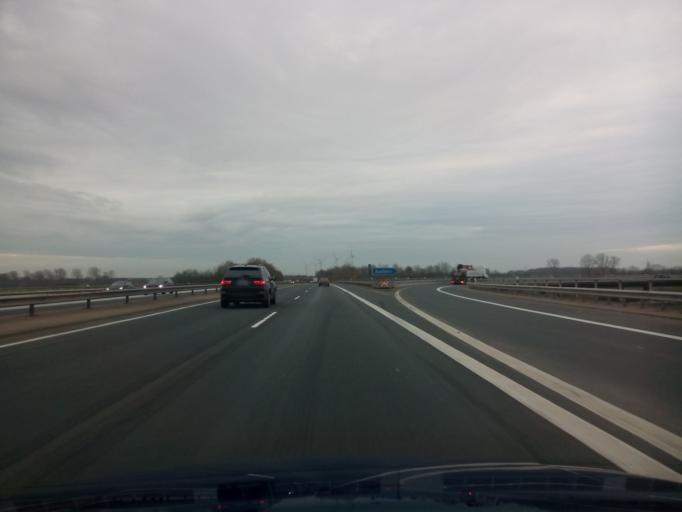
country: DE
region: Lower Saxony
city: Loxstedt
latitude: 53.4646
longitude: 8.6010
